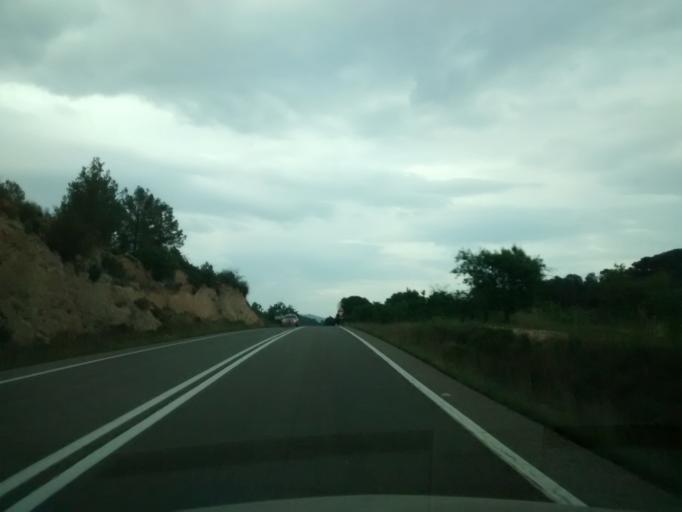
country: ES
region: Catalonia
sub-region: Provincia de Tarragona
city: Benifallet
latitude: 41.0104
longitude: 0.5040
